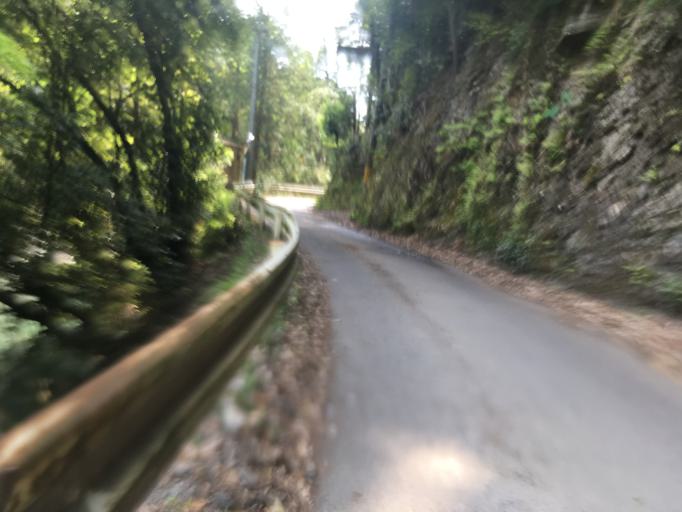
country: JP
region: Kyoto
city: Kameoka
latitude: 35.0270
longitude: 135.6464
